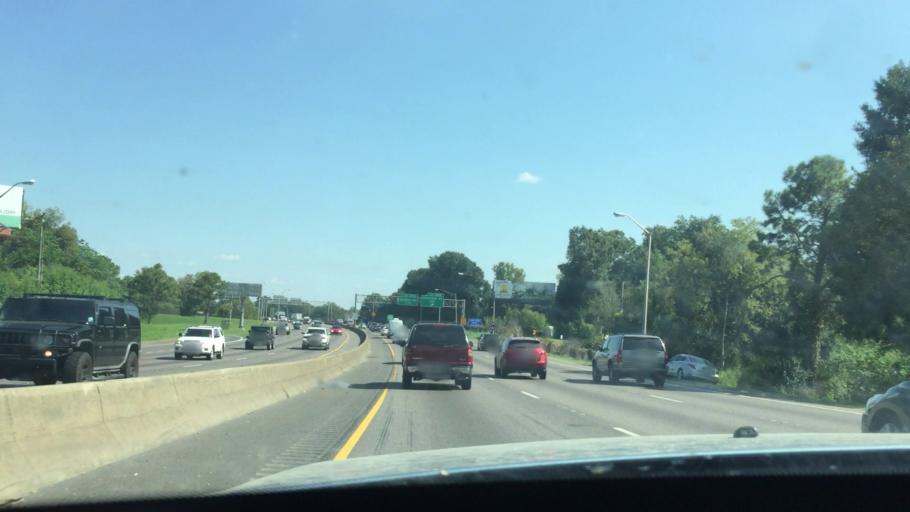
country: US
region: Louisiana
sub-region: East Baton Rouge Parish
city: Baton Rouge
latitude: 30.4293
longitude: -91.1725
